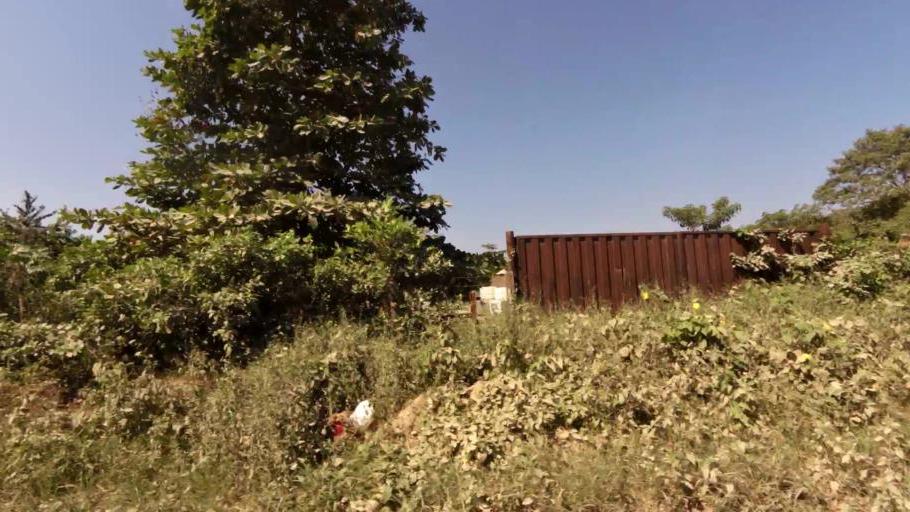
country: CO
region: Bolivar
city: Cartagena
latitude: 10.3555
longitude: -75.4887
